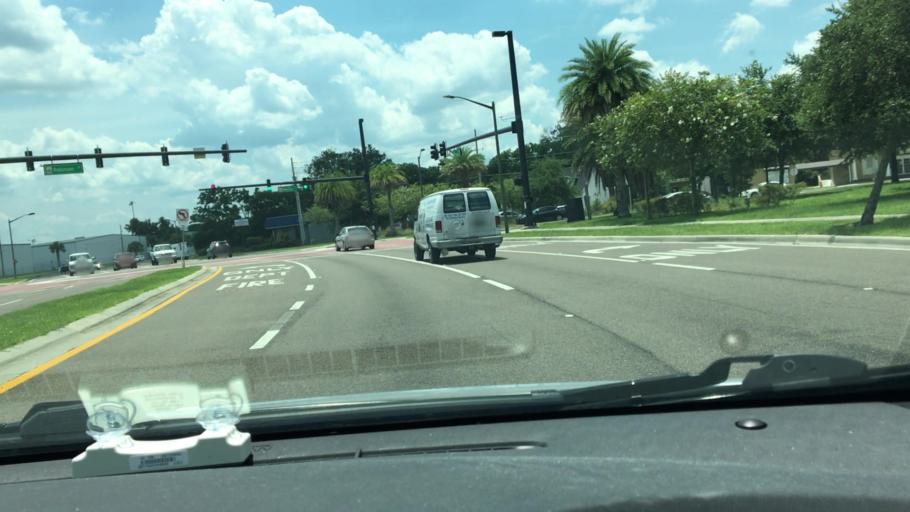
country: US
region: Florida
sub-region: Orange County
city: Orlando
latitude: 28.5469
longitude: -81.3454
